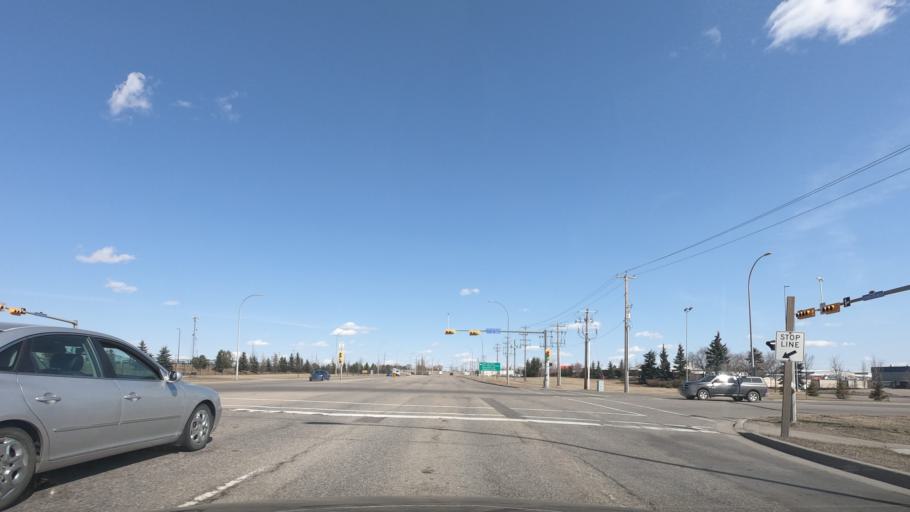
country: CA
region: Alberta
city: Airdrie
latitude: 51.2999
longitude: -113.9953
